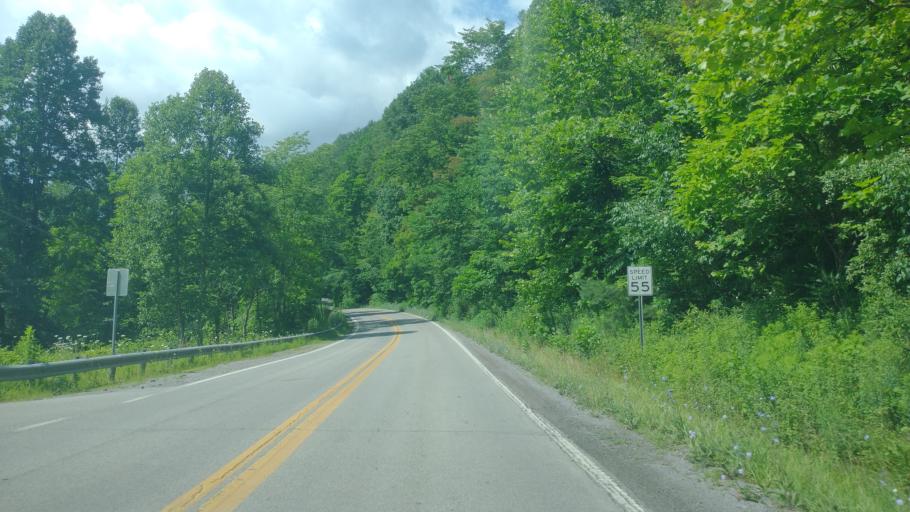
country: US
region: West Virginia
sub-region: McDowell County
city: Welch
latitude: 37.4282
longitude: -81.5104
